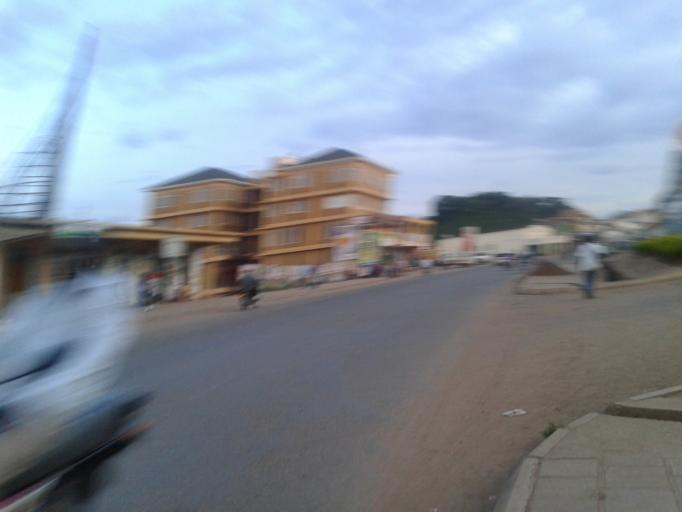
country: UG
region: Eastern Region
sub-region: Mbale District
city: Mbale
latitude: 1.0780
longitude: 34.1789
